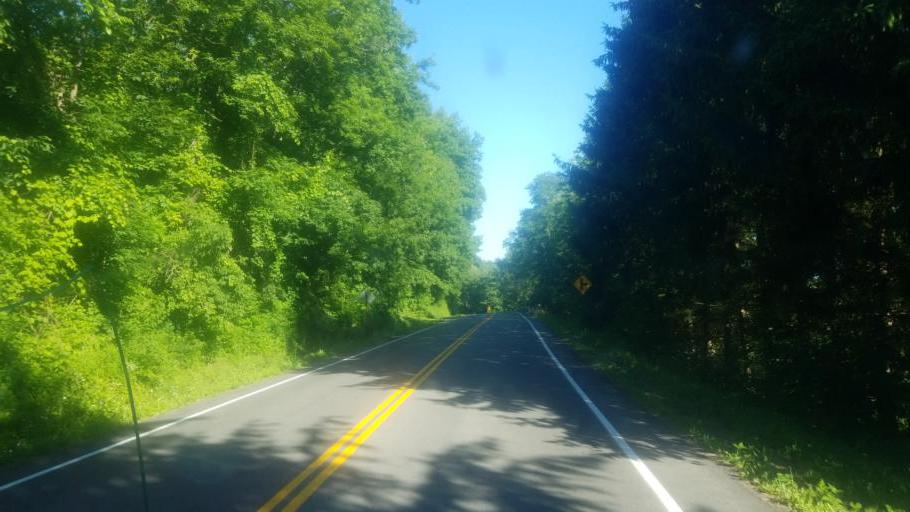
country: US
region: New York
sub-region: Wayne County
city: Newark
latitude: 43.0905
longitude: -77.0621
